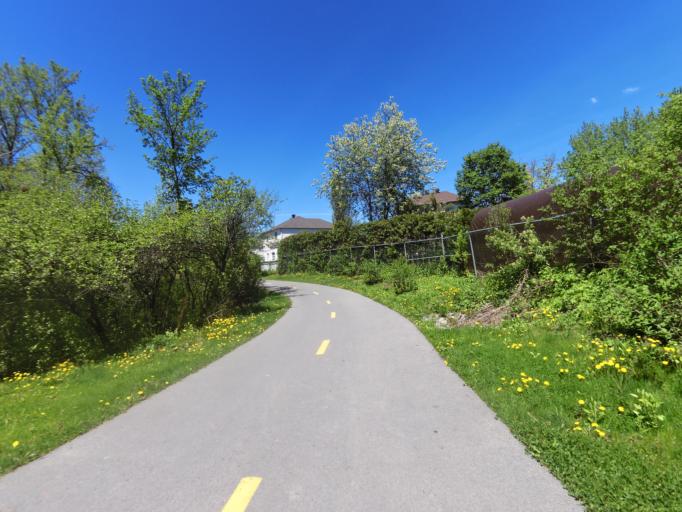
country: CA
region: Ontario
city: Ottawa
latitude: 45.4397
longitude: -75.7836
